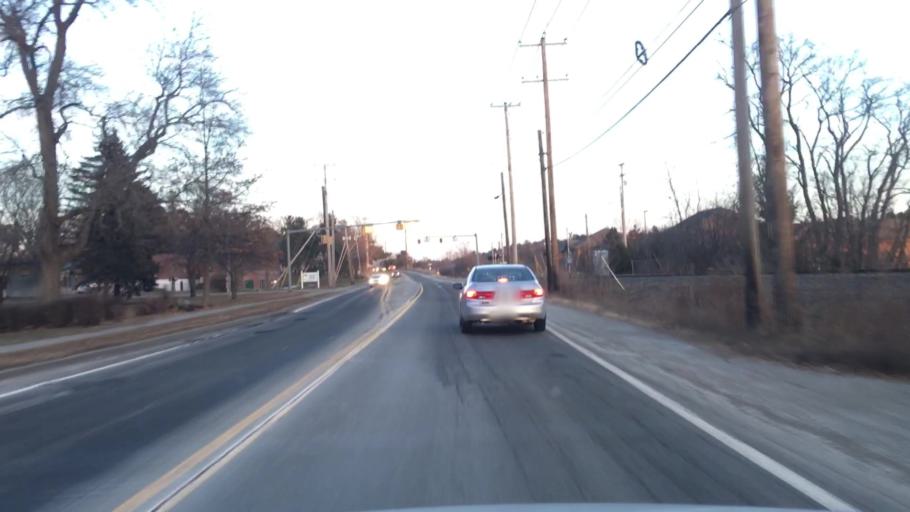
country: US
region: Maine
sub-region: Penobscot County
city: Brewer
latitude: 44.8113
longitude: -68.7449
